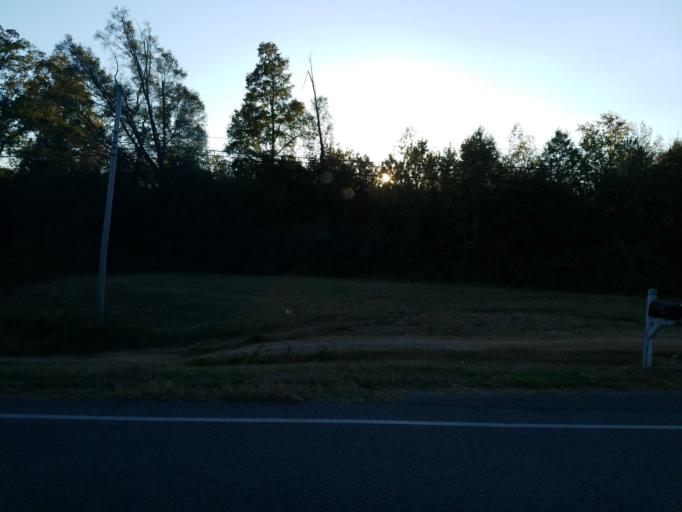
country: US
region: Georgia
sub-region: Gordon County
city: Calhoun
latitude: 34.5158
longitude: -84.9603
